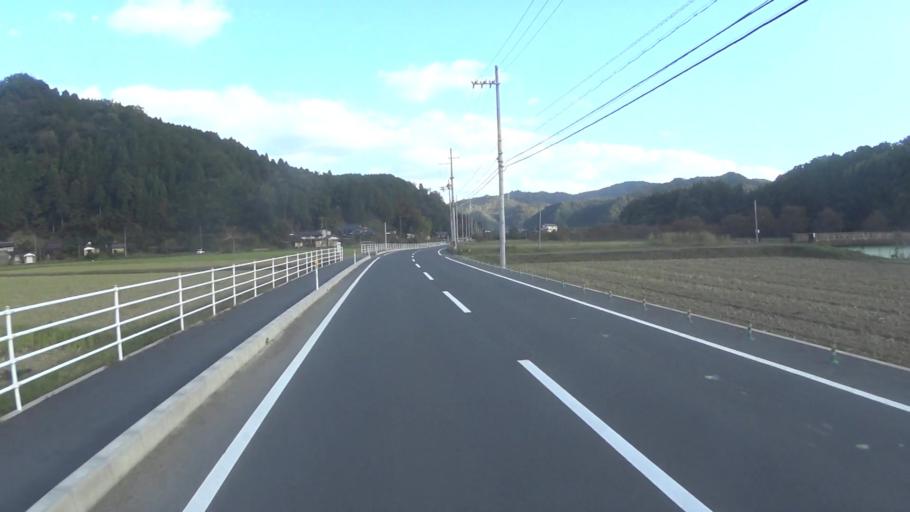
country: JP
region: Kyoto
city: Maizuru
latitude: 35.4337
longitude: 135.2265
